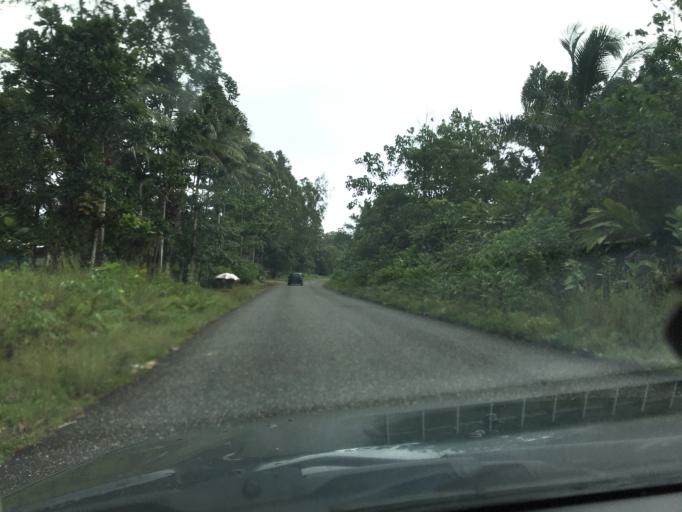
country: SB
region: Western Province
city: Gizo
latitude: -8.2381
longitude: 157.2245
